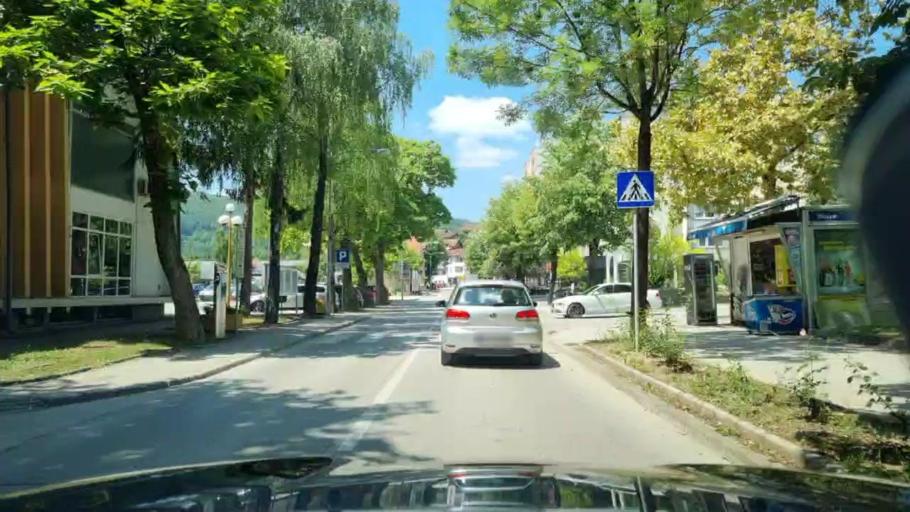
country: BA
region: Federation of Bosnia and Herzegovina
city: Kljuc
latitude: 44.5330
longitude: 16.7750
